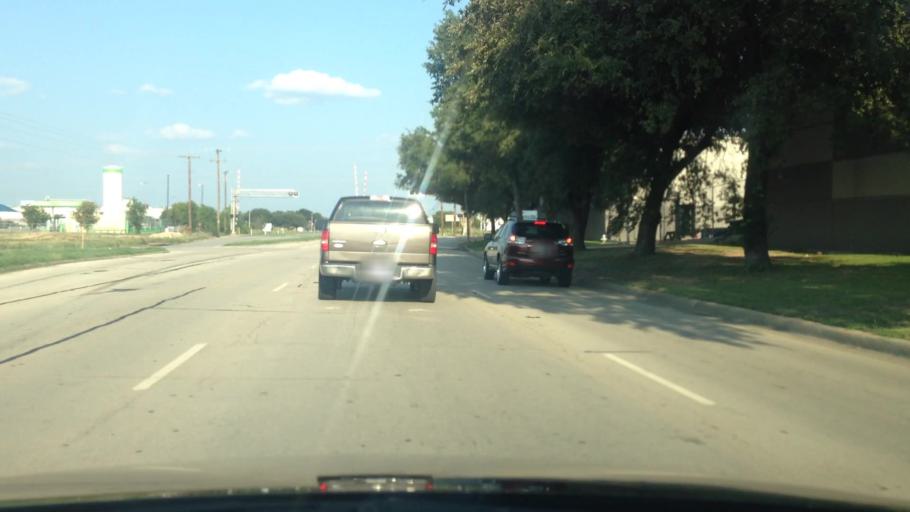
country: US
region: Texas
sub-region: Tarrant County
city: Everman
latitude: 32.6275
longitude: -97.3187
